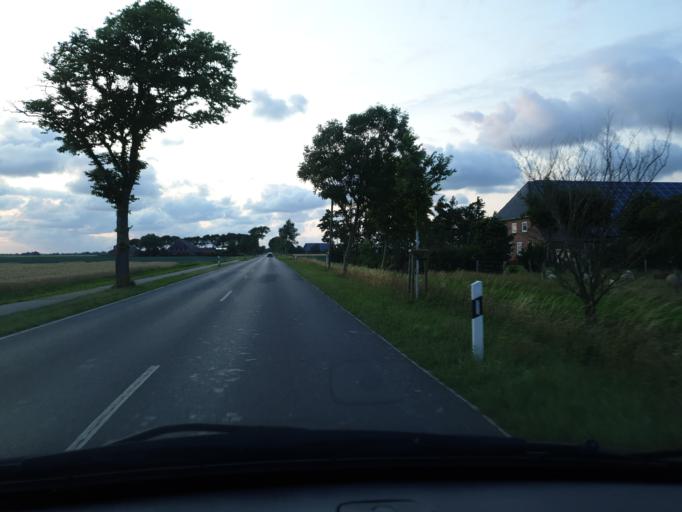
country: DE
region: Schleswig-Holstein
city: Friedrichskoog
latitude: 53.9769
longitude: 8.9206
